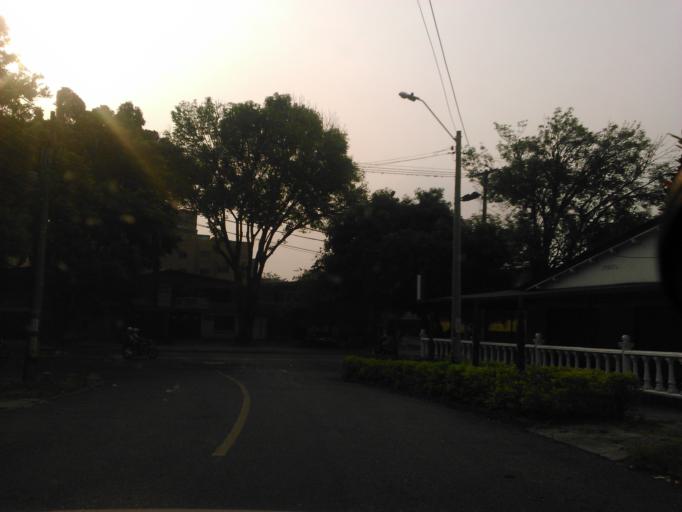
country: CO
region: Antioquia
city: Medellin
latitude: 6.2555
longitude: -75.5988
